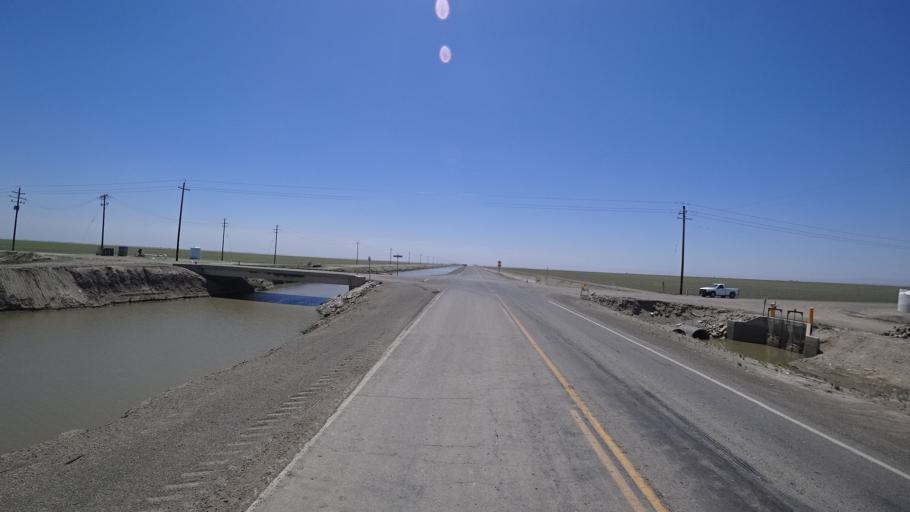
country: US
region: California
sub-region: Kings County
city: Corcoran
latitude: 36.0218
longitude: -119.6432
